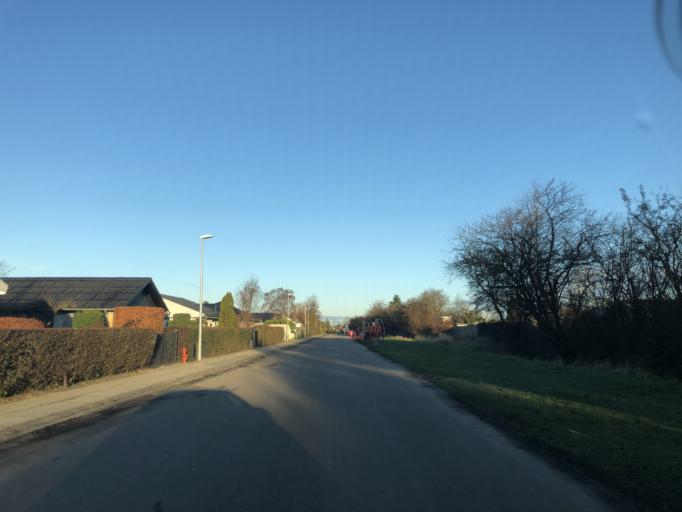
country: DK
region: Capital Region
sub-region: Tarnby Kommune
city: Tarnby
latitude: 55.5961
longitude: 12.5891
